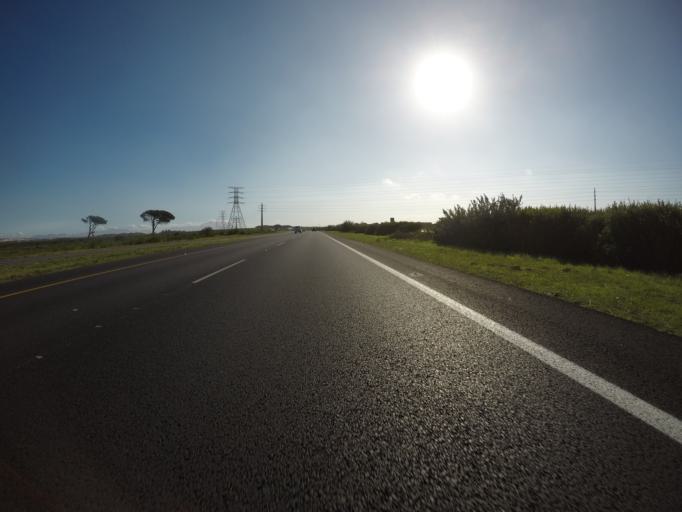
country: ZA
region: Western Cape
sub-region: Cape Winelands District Municipality
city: Stellenbosch
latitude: -34.0476
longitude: 18.7552
